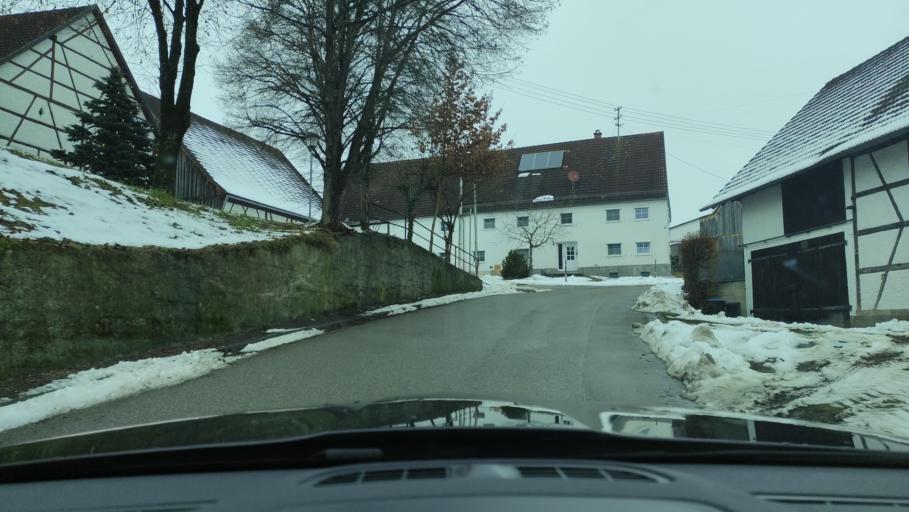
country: DE
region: Bavaria
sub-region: Swabia
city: Deisenhausen
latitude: 48.2824
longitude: 10.3304
